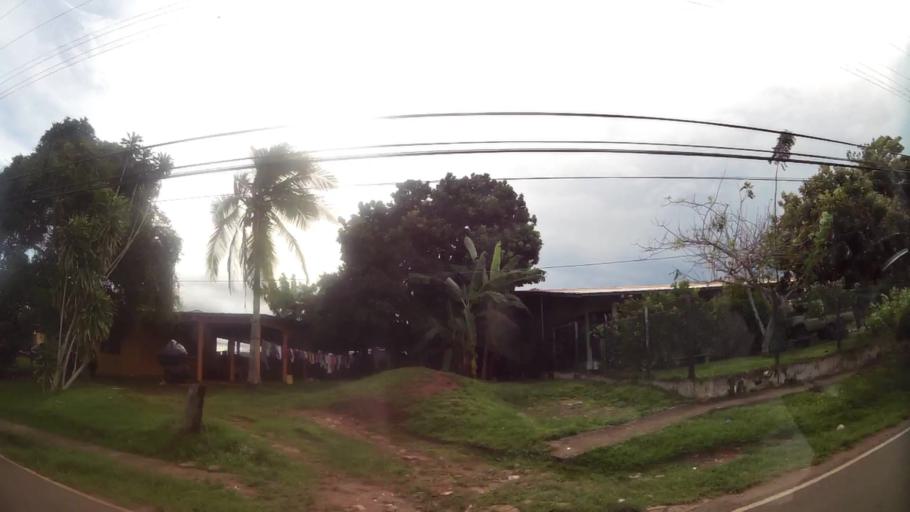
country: PA
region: Panama
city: El Coco
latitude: 8.8752
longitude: -79.8055
